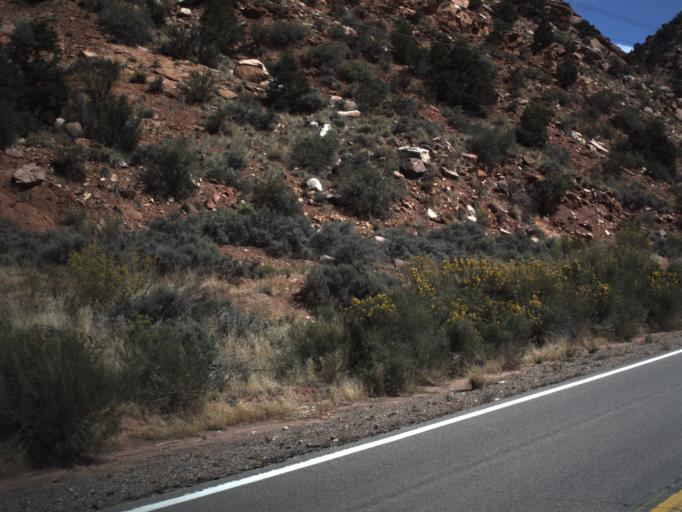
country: US
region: Utah
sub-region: Iron County
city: Cedar City
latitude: 37.6722
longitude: -113.0419
